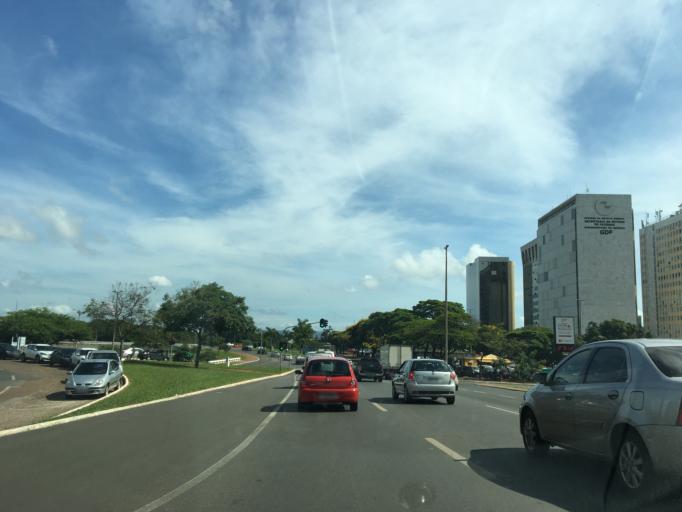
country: BR
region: Federal District
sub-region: Brasilia
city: Brasilia
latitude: -15.7900
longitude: -47.8809
